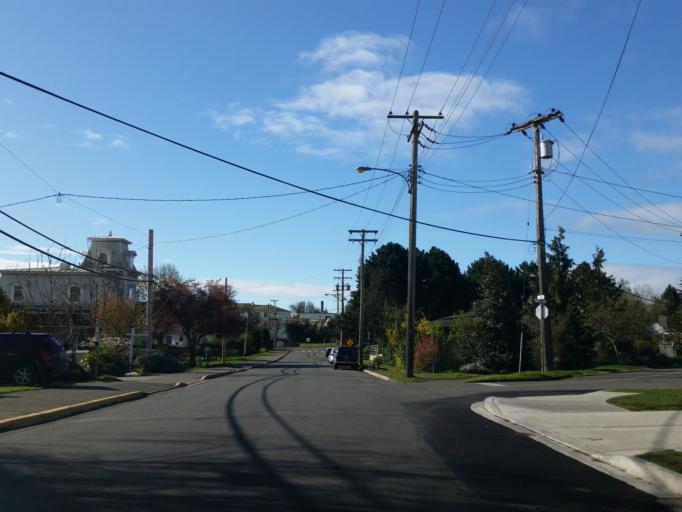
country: CA
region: British Columbia
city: Victoria
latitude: 48.4284
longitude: -123.3991
